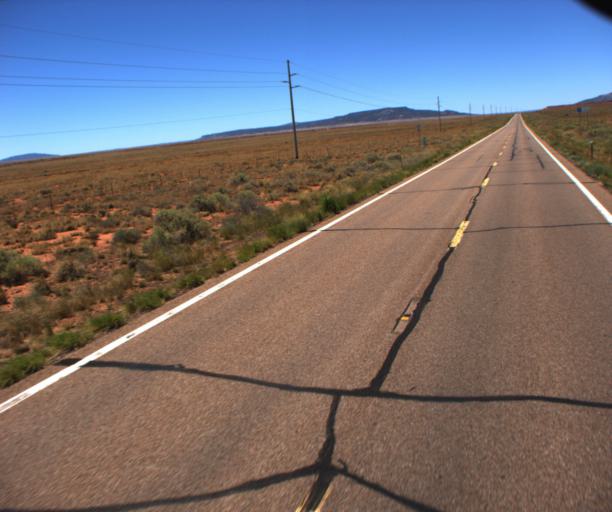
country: US
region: Arizona
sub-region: Coconino County
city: LeChee
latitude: 34.9378
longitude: -110.7849
